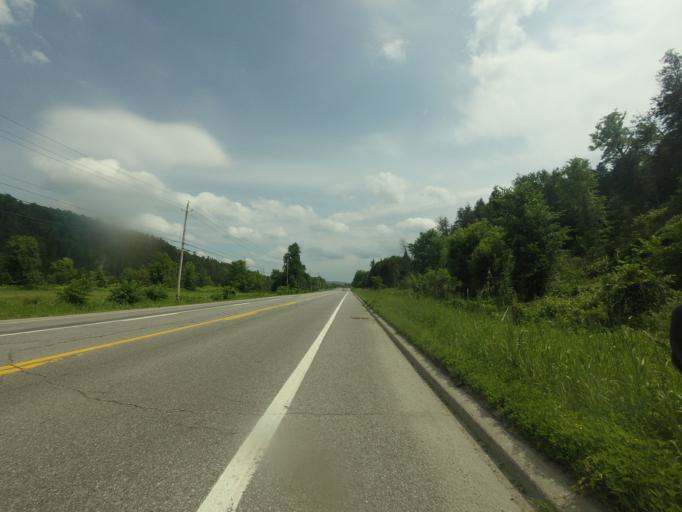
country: CA
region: Quebec
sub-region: Outaouais
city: Wakefield
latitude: 45.7551
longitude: -75.9174
